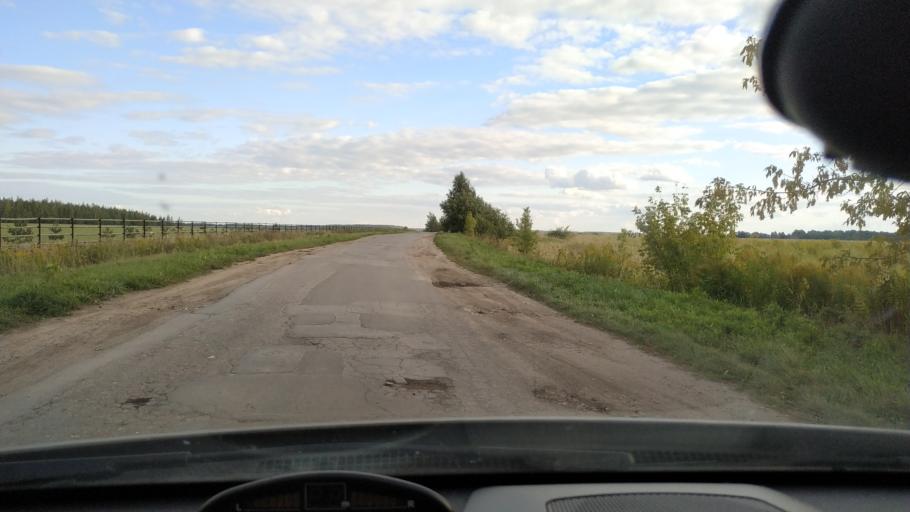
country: RU
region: Rjazan
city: Polyany
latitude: 54.5787
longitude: 39.8604
